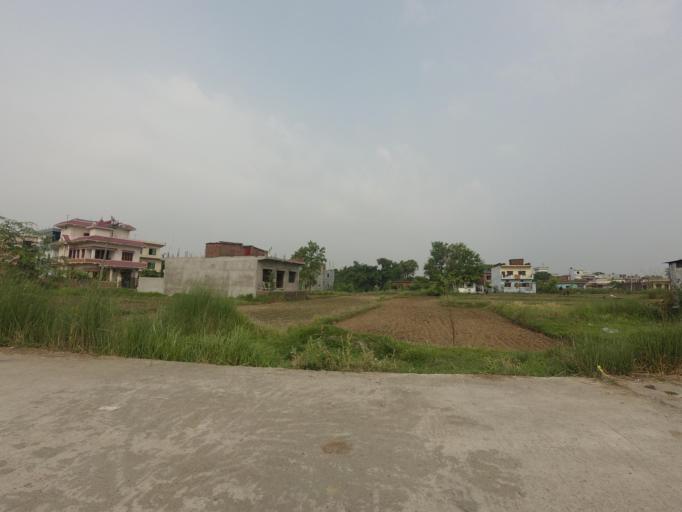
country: NP
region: Western Region
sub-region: Lumbini Zone
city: Bhairahawa
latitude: 27.4928
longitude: 83.4510
